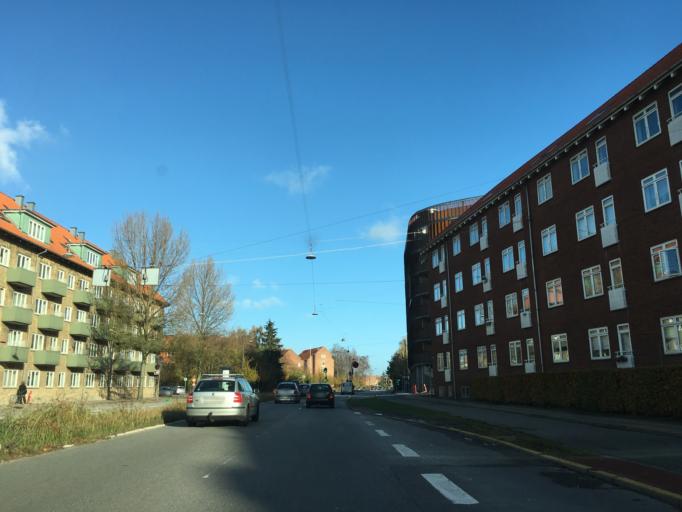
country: DK
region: Capital Region
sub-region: Frederiksberg Kommune
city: Frederiksberg
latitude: 55.7137
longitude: 12.5354
